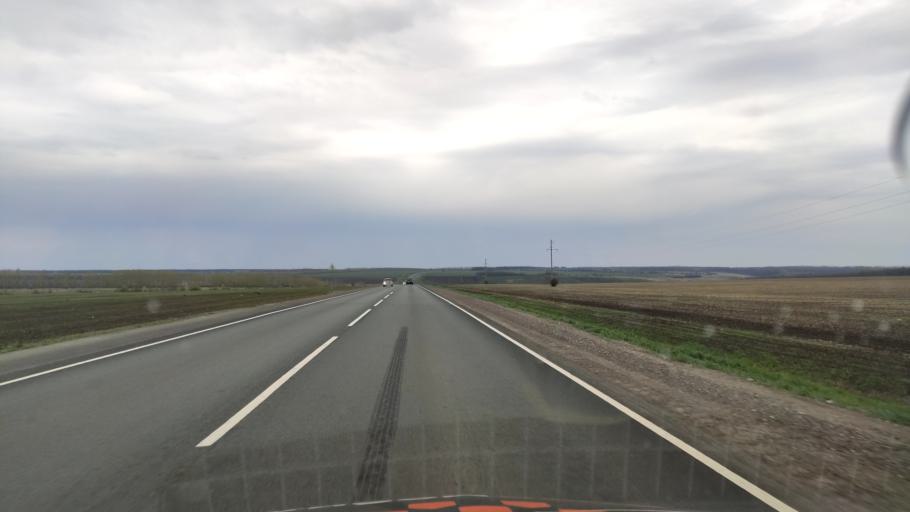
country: RU
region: Voronezj
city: Latnaya
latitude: 51.6434
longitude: 38.7072
